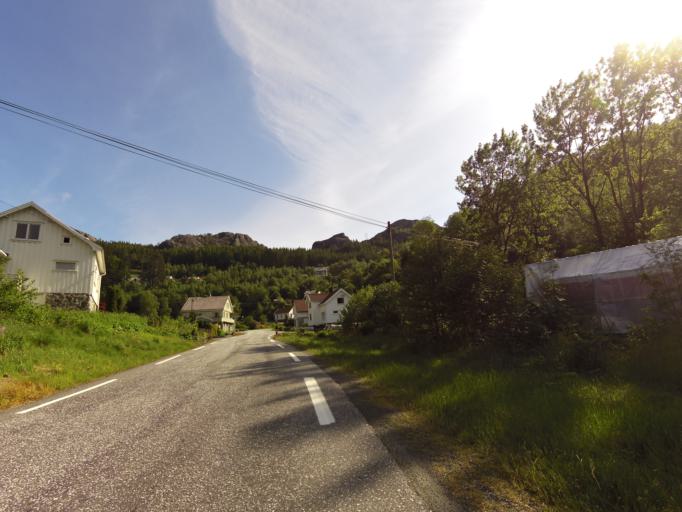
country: NO
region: Rogaland
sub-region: Sokndal
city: Hauge i Dalane
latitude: 58.3172
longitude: 6.3452
